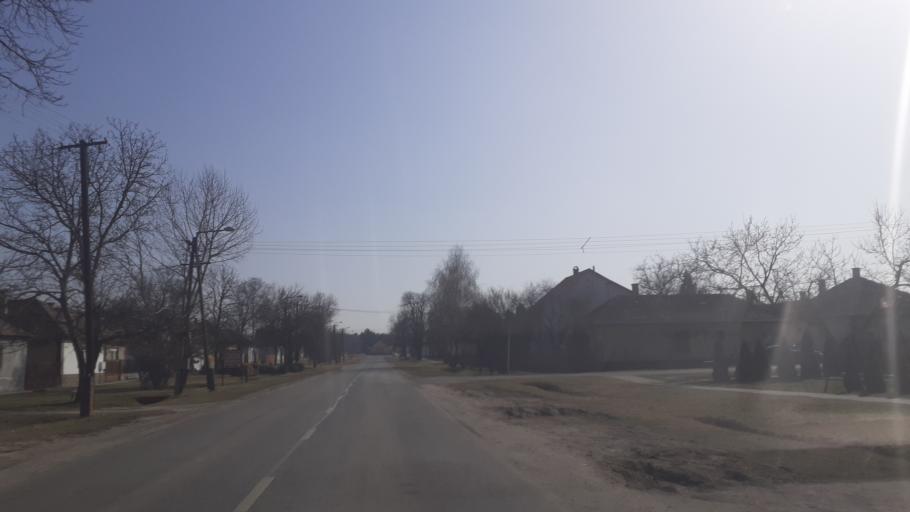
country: HU
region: Pest
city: Orkeny
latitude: 47.0803
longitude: 19.3714
